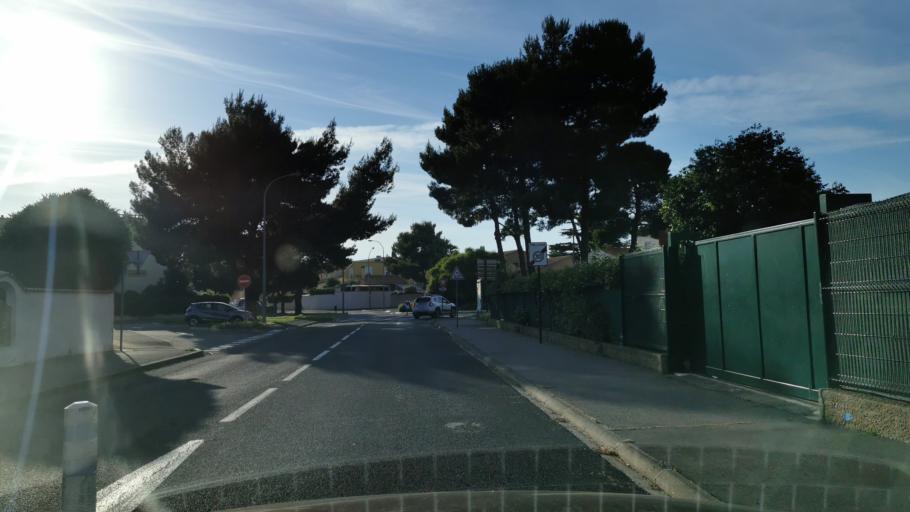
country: FR
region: Languedoc-Roussillon
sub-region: Departement de l'Aude
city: Narbonne
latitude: 43.1855
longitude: 3.0211
